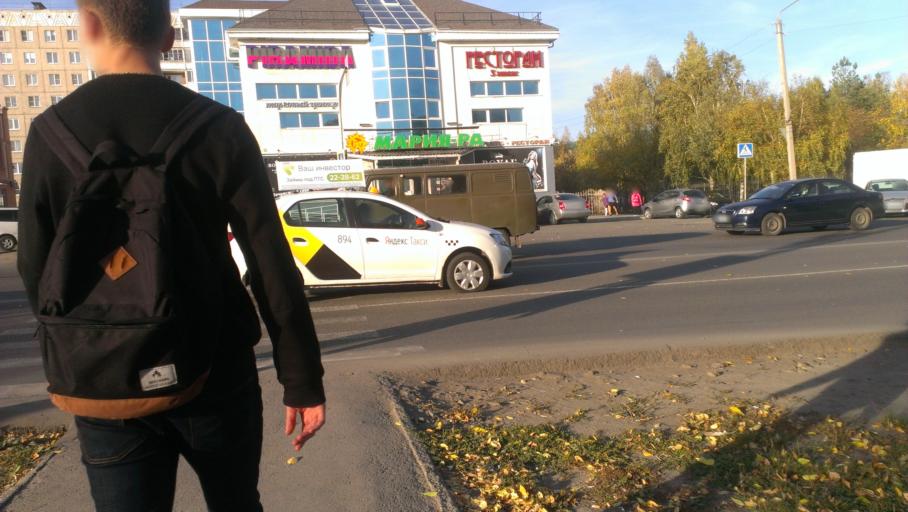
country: RU
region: Altai Krai
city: Novosilikatnyy
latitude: 53.3553
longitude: 83.6774
